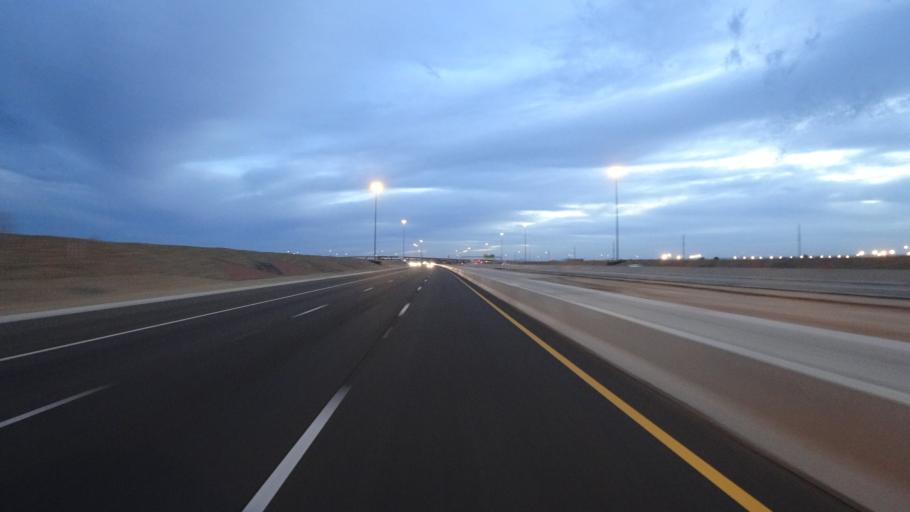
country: US
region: Arizona
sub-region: Maricopa County
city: Litchfield Park
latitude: 33.4748
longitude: -112.4250
